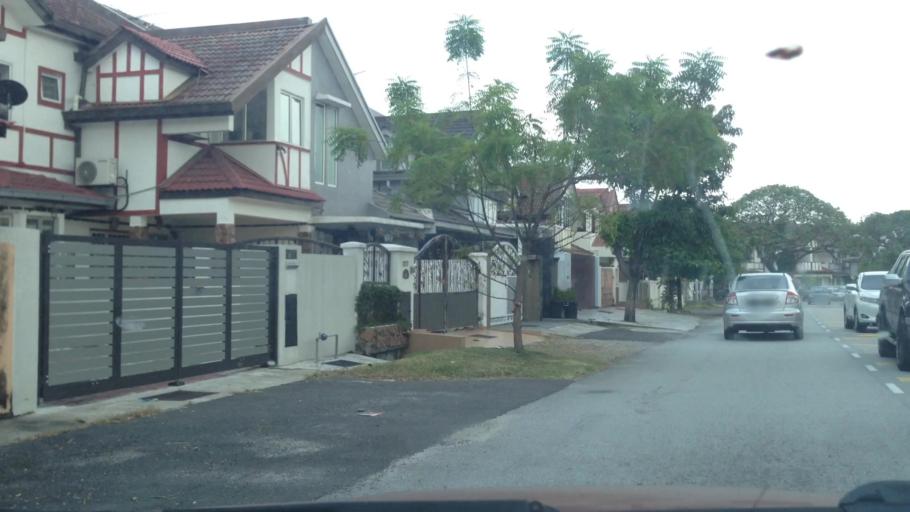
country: MY
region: Selangor
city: Subang Jaya
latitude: 3.0381
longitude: 101.5761
